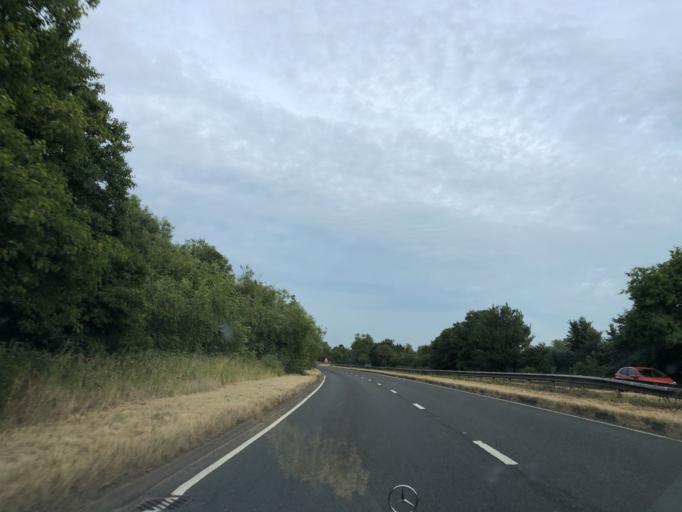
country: GB
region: England
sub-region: Solihull
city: Hampton in Arden
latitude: 52.4387
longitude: -1.6820
